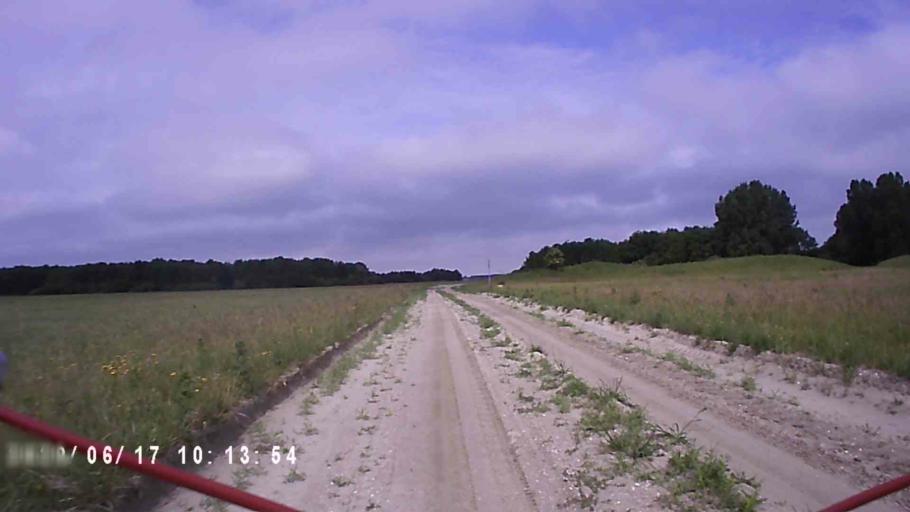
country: NL
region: Groningen
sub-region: Gemeente De Marne
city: Ulrum
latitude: 53.3835
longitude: 6.2624
